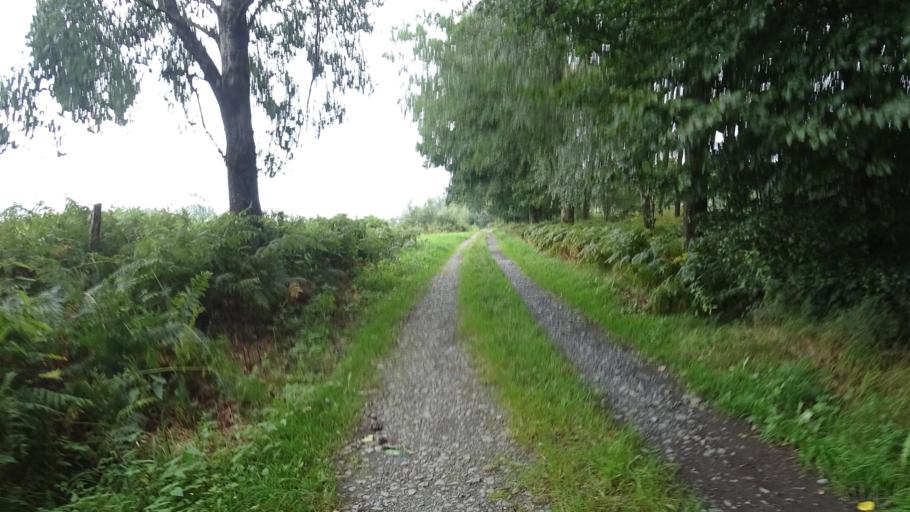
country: BE
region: Wallonia
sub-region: Province du Luxembourg
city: Chiny
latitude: 49.7958
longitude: 5.3300
